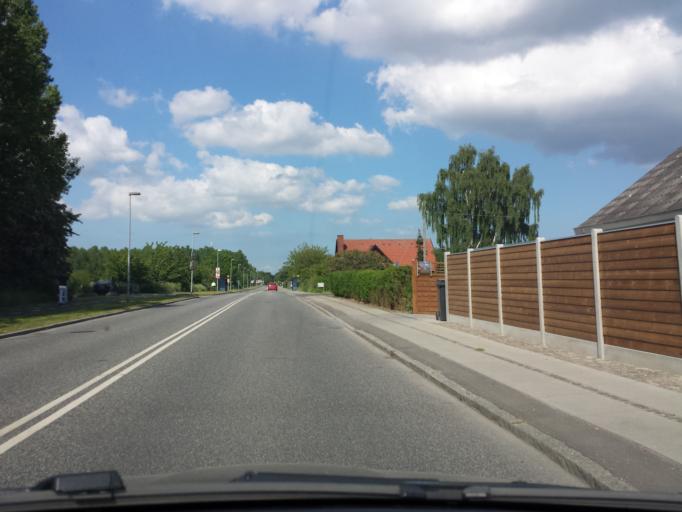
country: DK
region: Capital Region
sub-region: Ballerup Kommune
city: Ballerup
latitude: 55.7140
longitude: 12.3845
